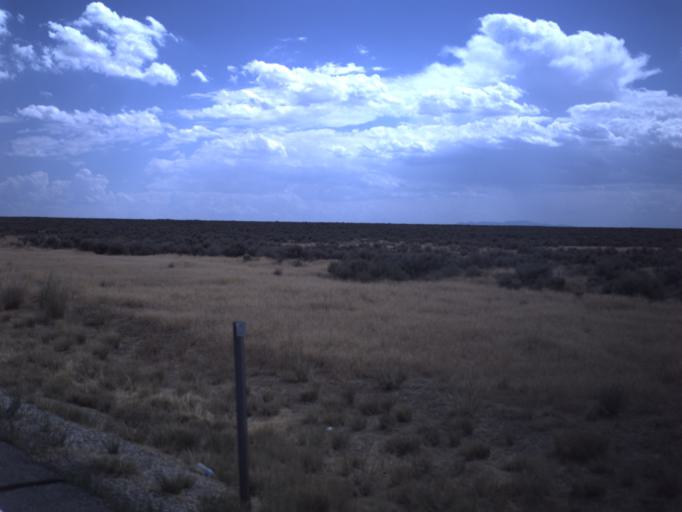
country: US
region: Utah
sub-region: Tooele County
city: Tooele
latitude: 40.3666
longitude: -112.3456
